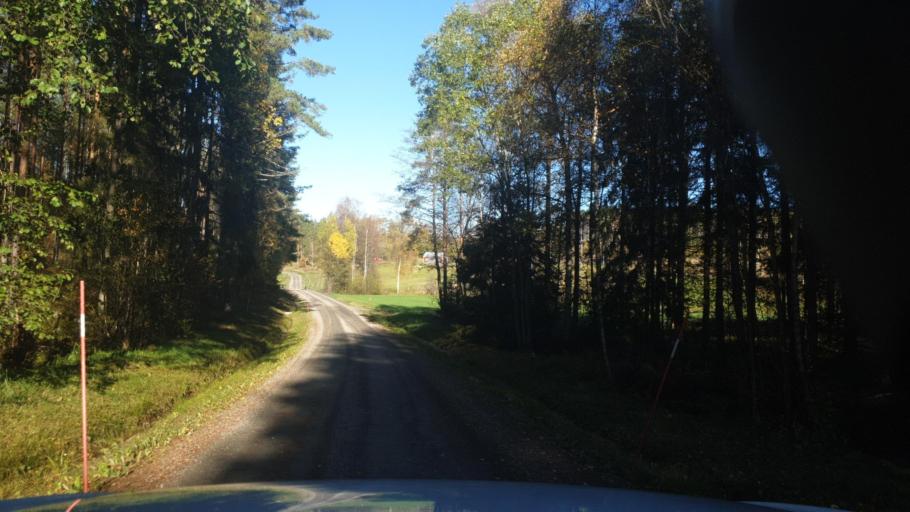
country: SE
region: Vaermland
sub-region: Arvika Kommun
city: Arvika
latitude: 59.5025
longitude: 12.7350
